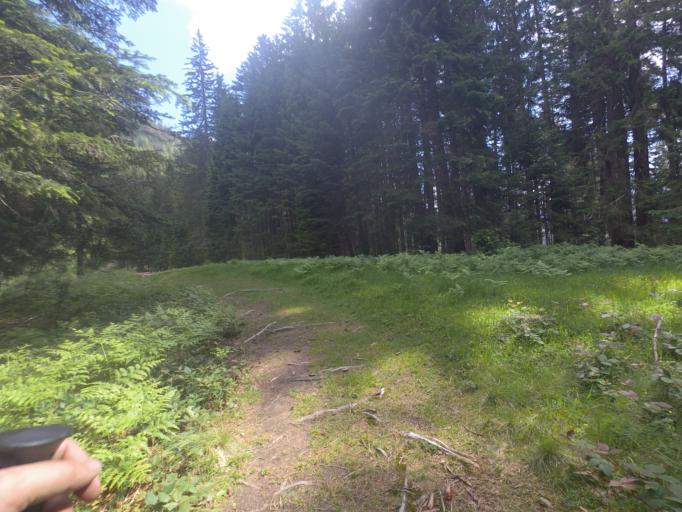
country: AT
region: Salzburg
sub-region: Politischer Bezirk Zell am See
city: Leogang
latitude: 47.4571
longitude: 12.7689
